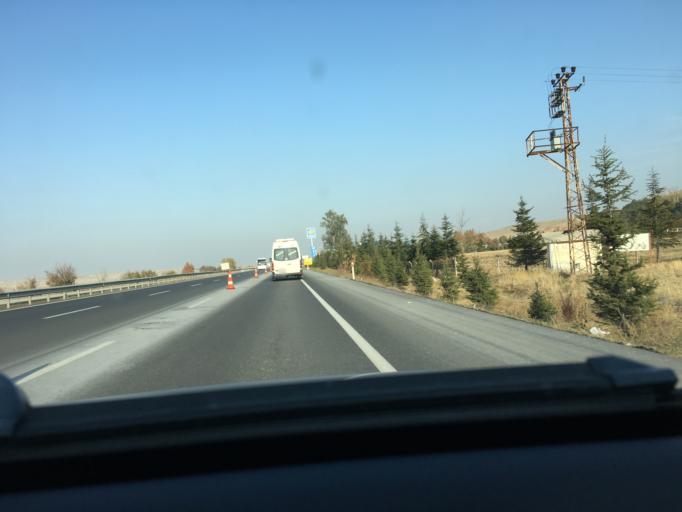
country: TR
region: Ankara
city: Temelli
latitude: 39.6933
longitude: 32.2581
